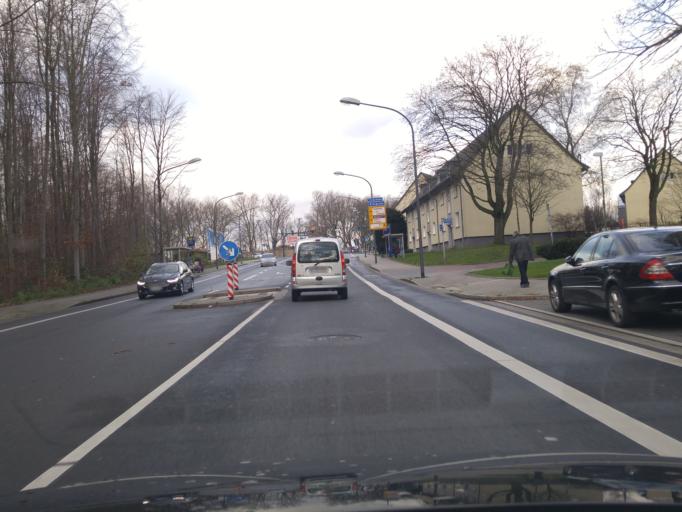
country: DE
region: North Rhine-Westphalia
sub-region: Regierungsbezirk Dusseldorf
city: Essen
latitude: 51.4565
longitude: 7.0673
